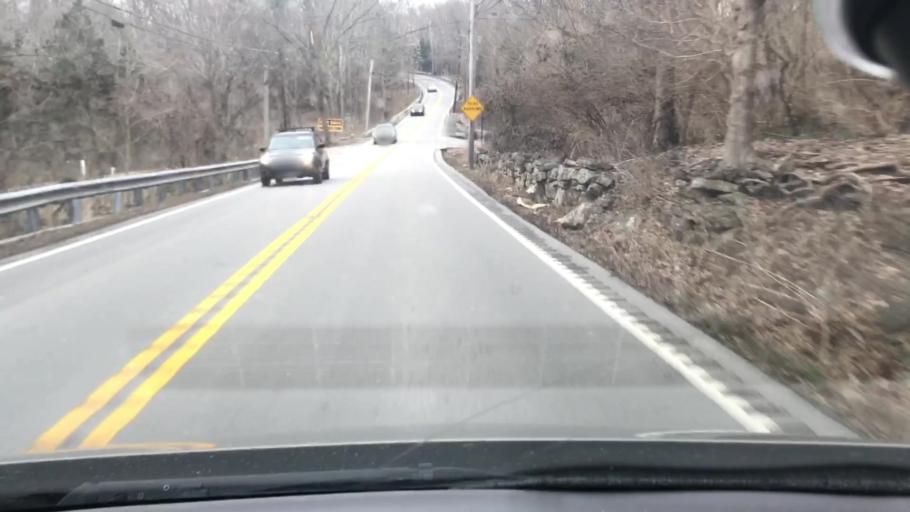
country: US
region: Kentucky
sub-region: Jefferson County
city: Barbourmeade
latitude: 38.2925
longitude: -85.6094
